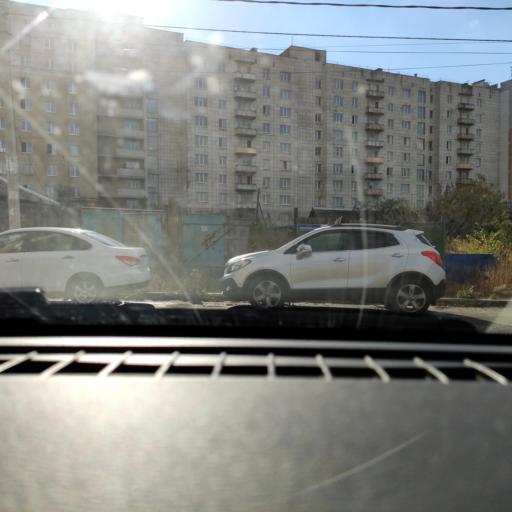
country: RU
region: Voronezj
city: Voronezh
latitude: 51.6782
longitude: 39.2484
